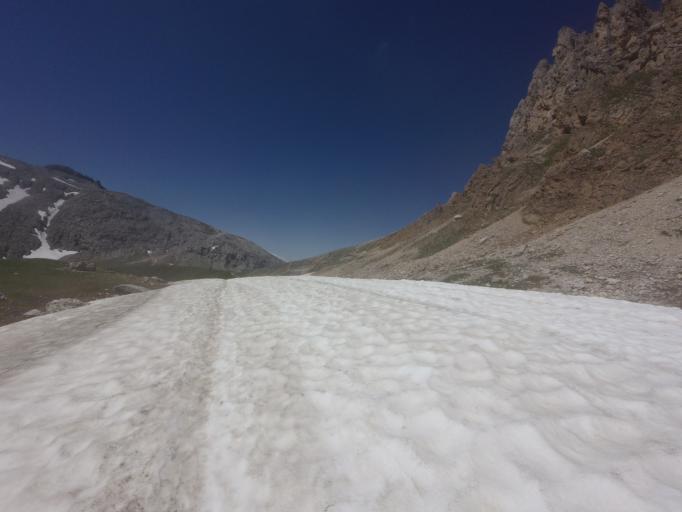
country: IT
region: Trentino-Alto Adige
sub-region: Provincia di Trento
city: Mazzin
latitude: 46.4985
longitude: 11.6354
